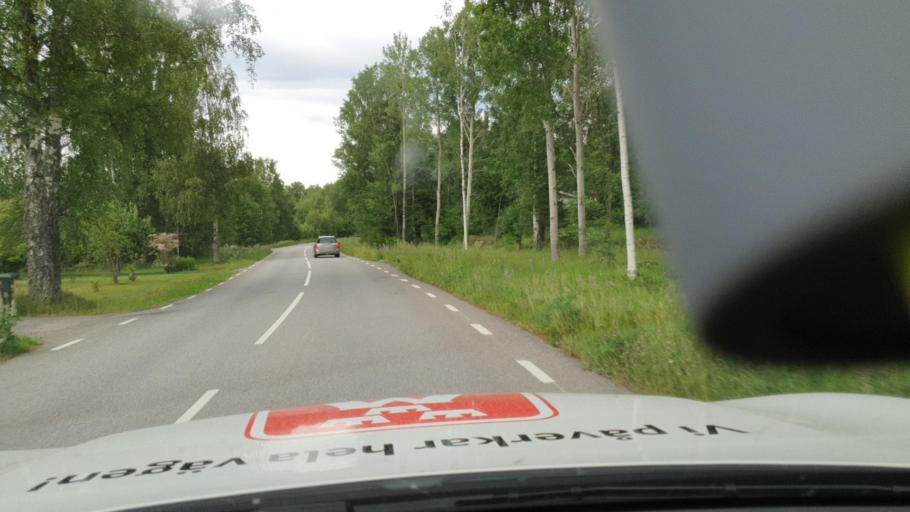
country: SE
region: Vaestra Goetaland
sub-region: Karlsborgs Kommun
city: Karlsborg
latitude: 58.7492
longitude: 14.5087
